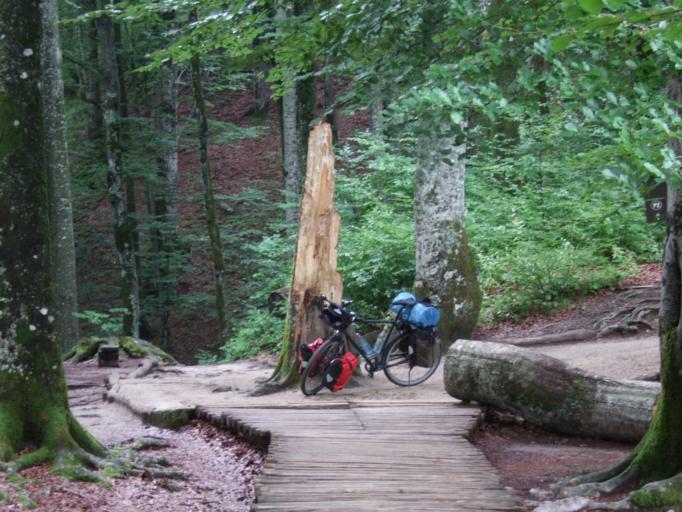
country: HR
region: Licko-Senjska
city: Jezerce
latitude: 44.8715
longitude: 15.6043
